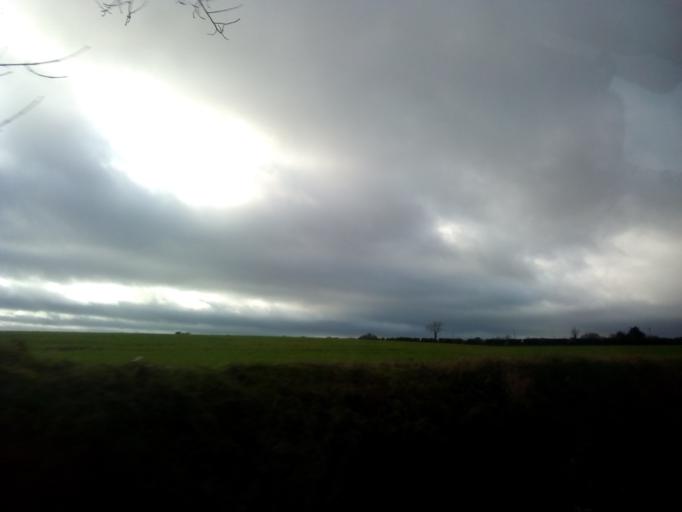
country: IE
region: Leinster
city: Lusk
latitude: 53.5595
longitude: -6.1410
